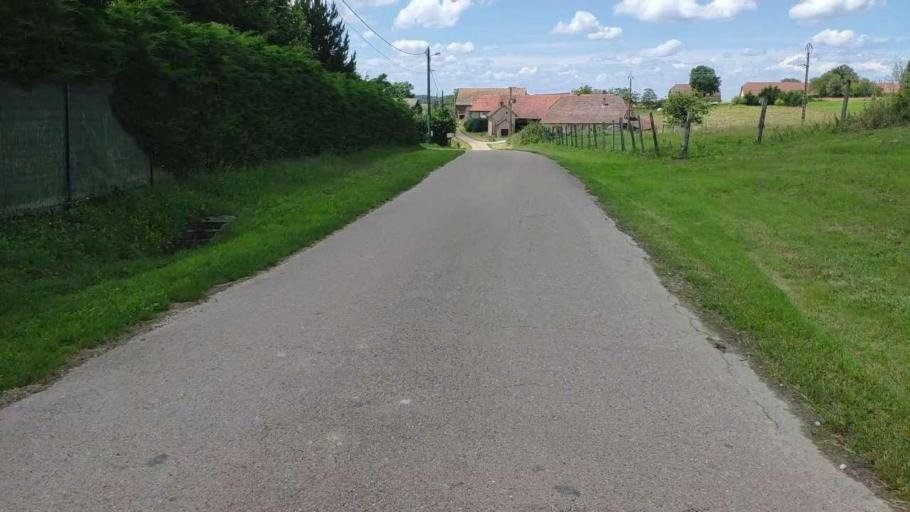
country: FR
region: Franche-Comte
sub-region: Departement du Jura
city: Bletterans
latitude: 46.8484
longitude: 5.4444
